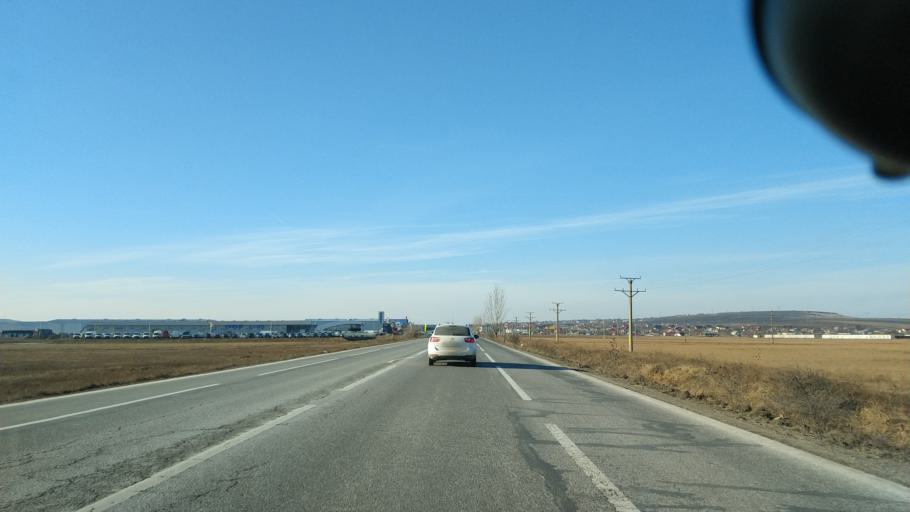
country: RO
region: Iasi
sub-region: Comuna Letcani
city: Letcani
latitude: 47.1878
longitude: 27.4407
